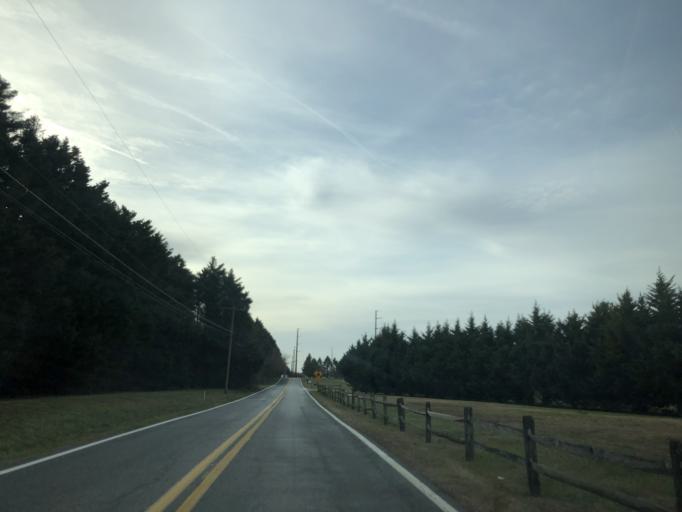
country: US
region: Delaware
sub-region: New Castle County
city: Townsend
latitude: 39.4488
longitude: -75.6300
